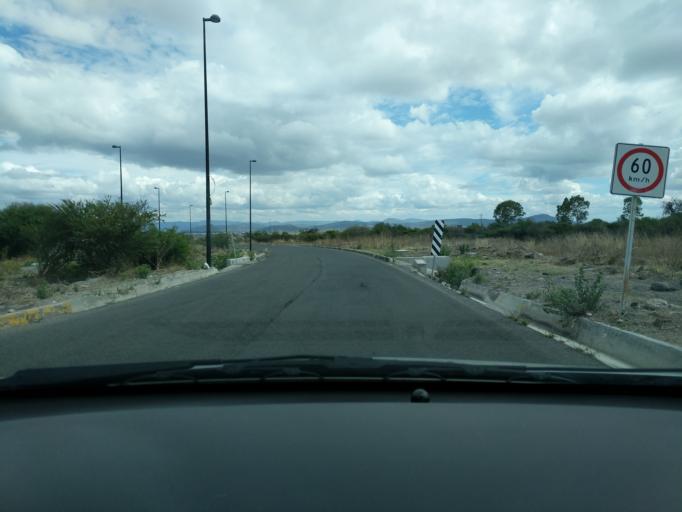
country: MX
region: Queretaro
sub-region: El Marques
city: La Pradera
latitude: 20.6671
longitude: -100.3161
